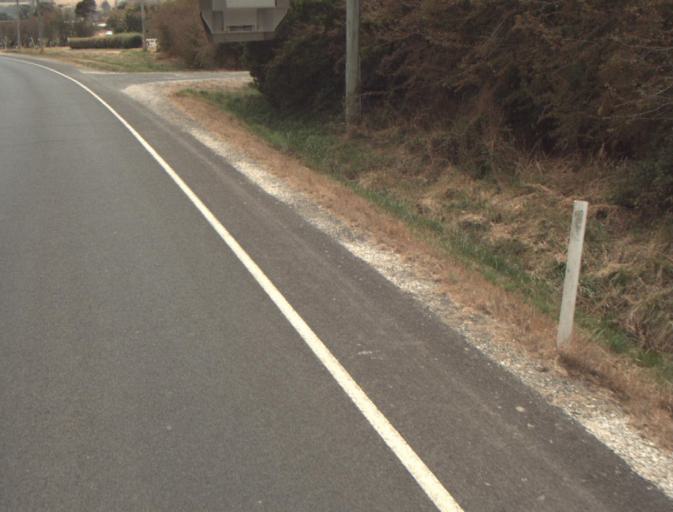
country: AU
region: Tasmania
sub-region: Launceston
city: Mayfield
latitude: -41.2596
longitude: 147.2181
